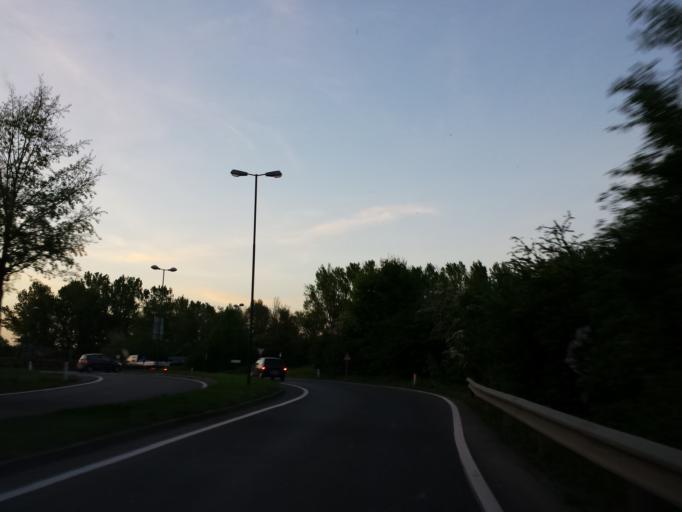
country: AT
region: Lower Austria
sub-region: Politischer Bezirk Tulln
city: Tulln
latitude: 48.3395
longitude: 16.0599
